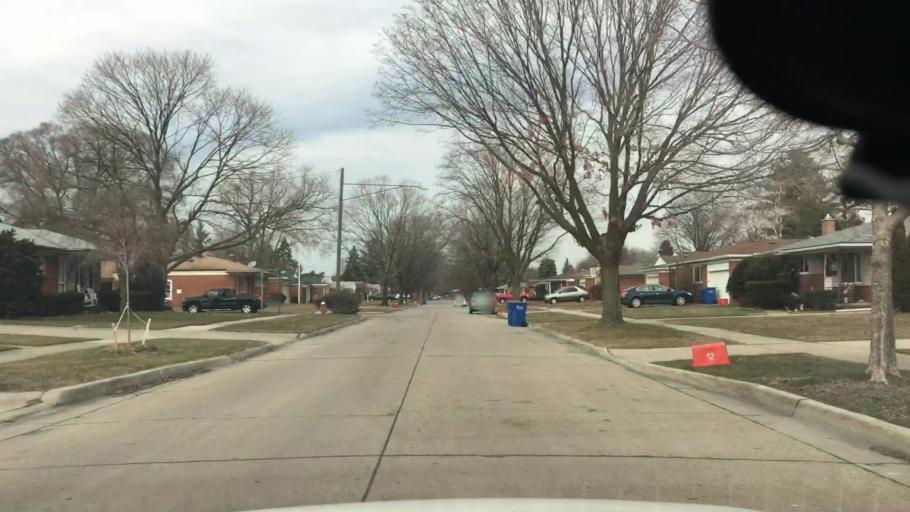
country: US
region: Michigan
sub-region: Oakland County
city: Madison Heights
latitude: 42.4918
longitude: -83.0712
